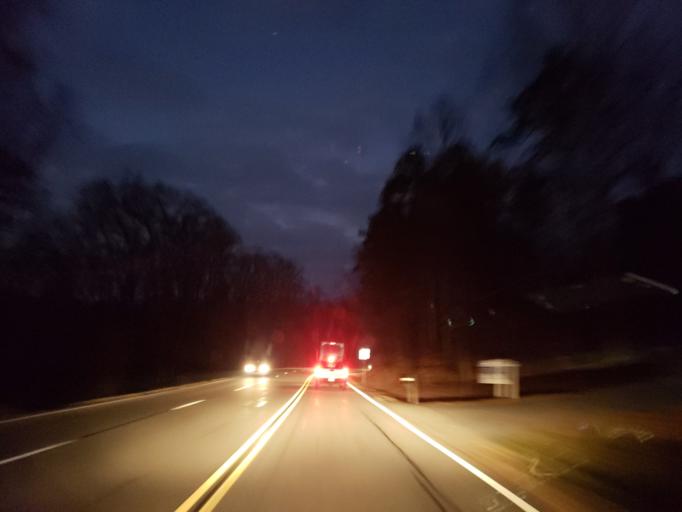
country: US
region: Georgia
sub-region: Polk County
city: Rockmart
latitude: 33.9565
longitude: -84.9983
